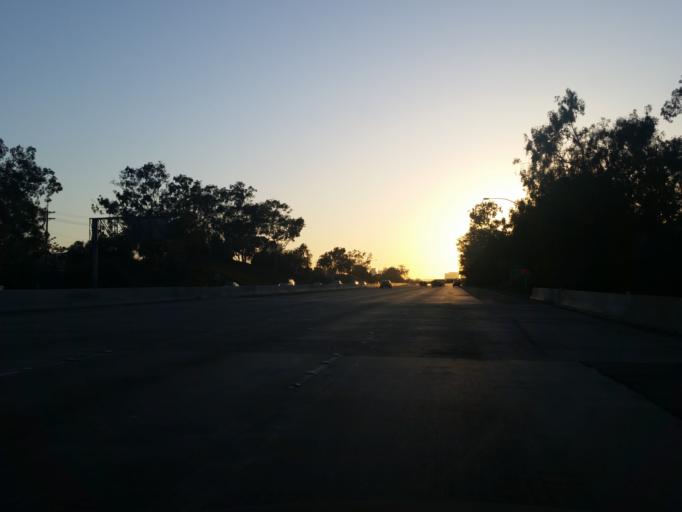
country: US
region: California
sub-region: San Diego County
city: San Diego
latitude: 32.7134
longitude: -117.1335
